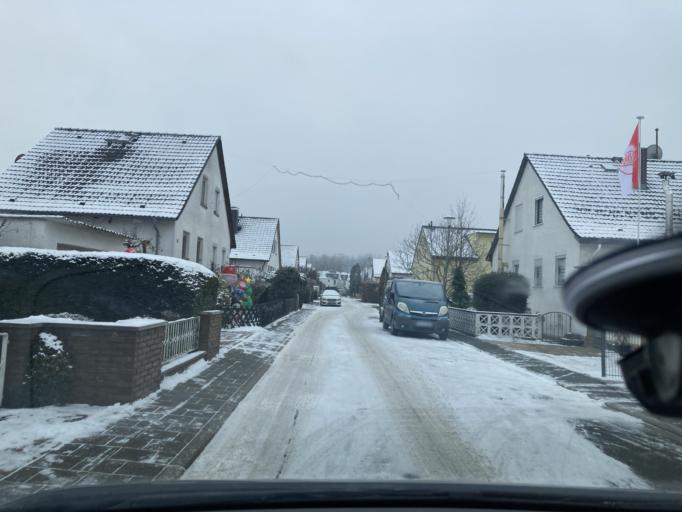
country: DE
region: Hesse
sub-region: Regierungsbezirk Darmstadt
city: Offenbach
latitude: 50.0860
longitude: 8.7800
